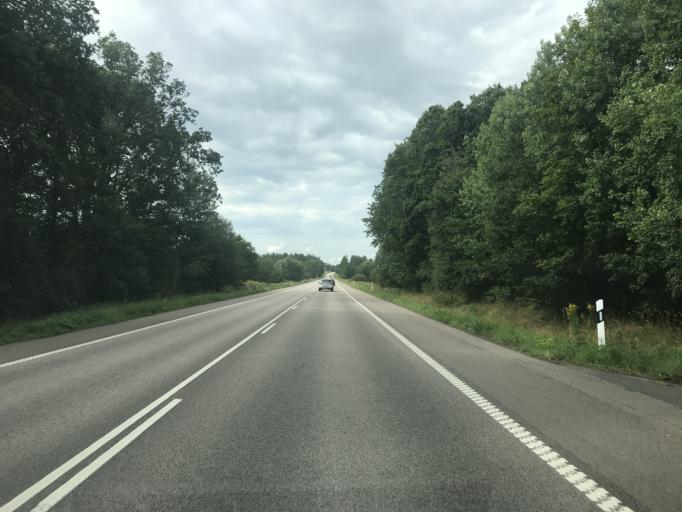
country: SE
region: Skane
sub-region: Hassleholms Kommun
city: Hassleholm
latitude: 56.1303
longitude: 13.8224
